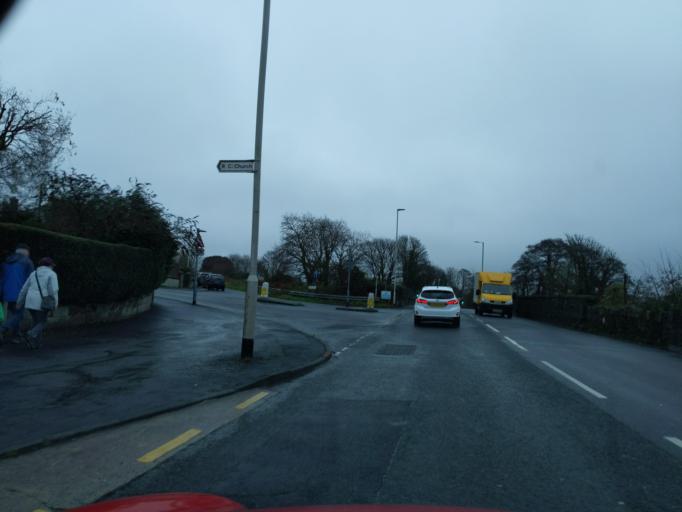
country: GB
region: England
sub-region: Devon
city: Plympton
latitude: 50.3895
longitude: -4.0642
